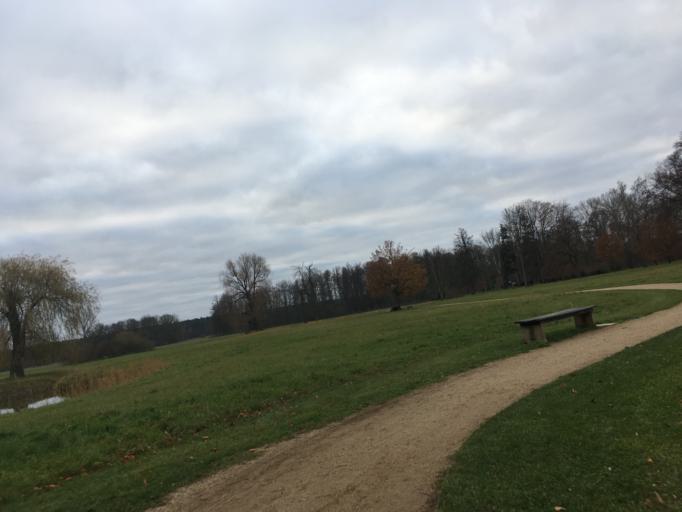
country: DE
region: Brandenburg
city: Neuhardenberg
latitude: 52.5908
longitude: 14.2467
